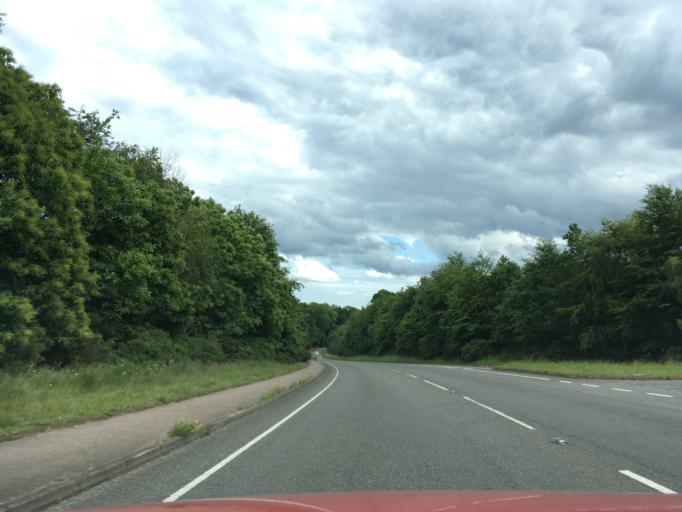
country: GB
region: England
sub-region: Central Bedfordshire
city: Aspley Guise
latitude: 52.0001
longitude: -0.6407
